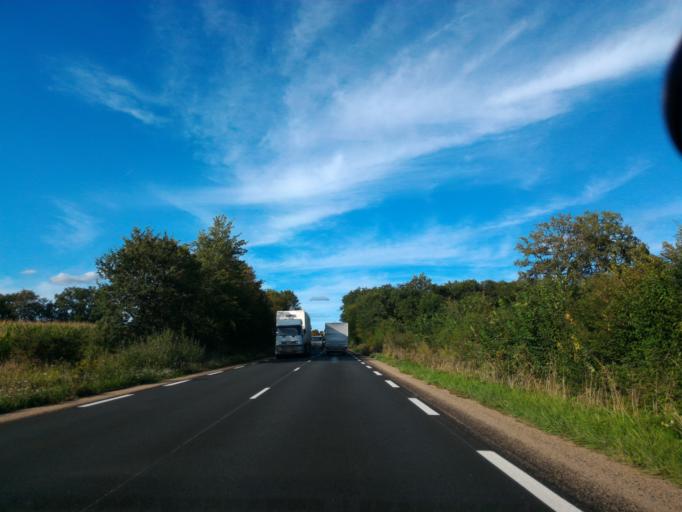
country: FR
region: Limousin
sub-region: Departement de la Haute-Vienne
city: Magnac-Laval
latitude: 46.1728
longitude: 1.1495
